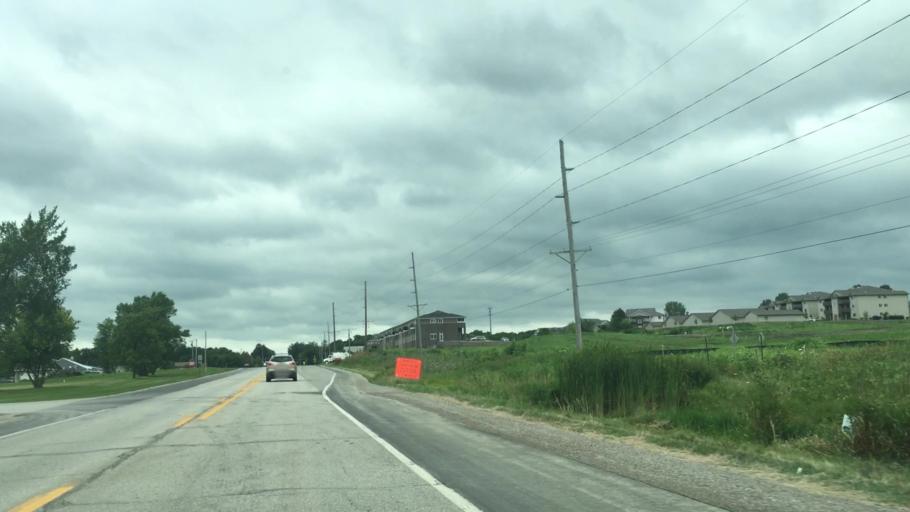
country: US
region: Iowa
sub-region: Johnson County
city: Tiffin
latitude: 41.7065
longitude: -91.6545
